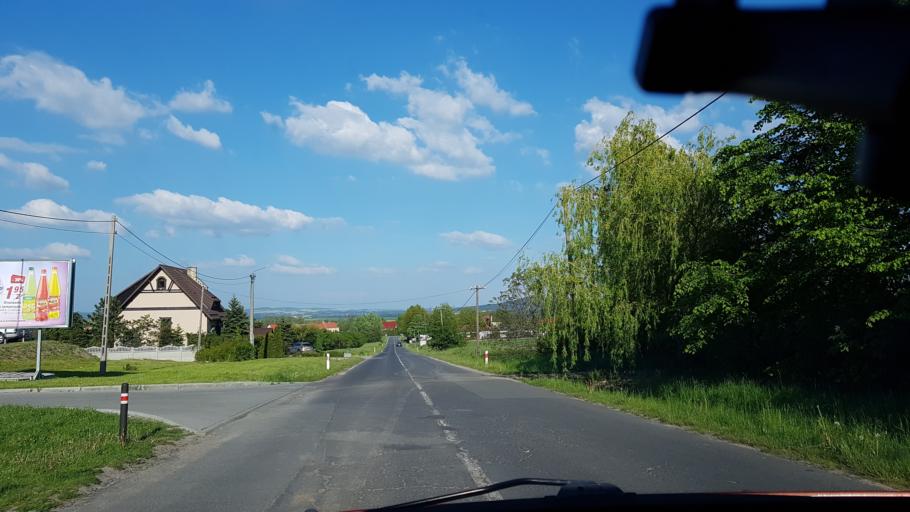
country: PL
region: Lower Silesian Voivodeship
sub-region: Powiat zabkowicki
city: Budzow
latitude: 50.5755
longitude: 16.6717
